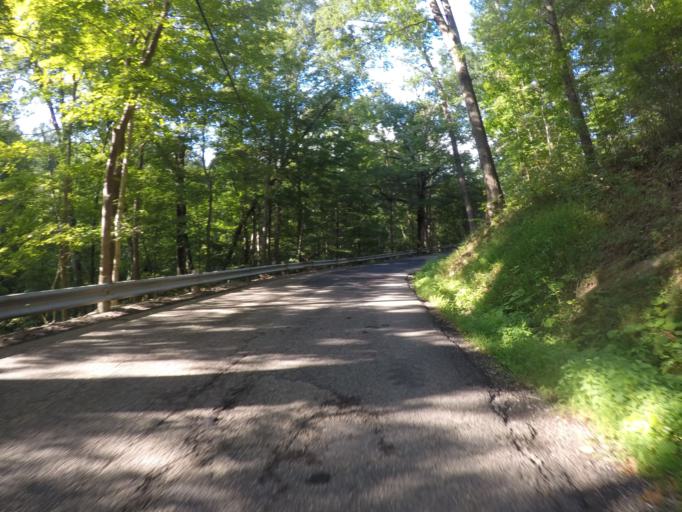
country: US
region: West Virginia
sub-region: Cabell County
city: Huntington
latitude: 38.4552
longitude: -82.4619
